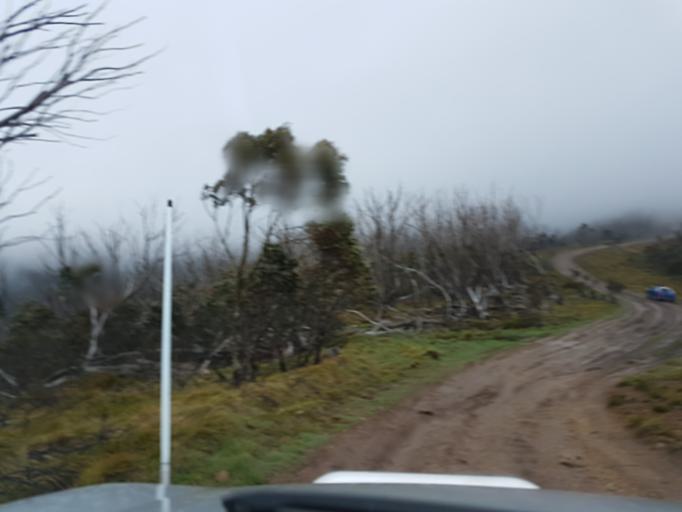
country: AU
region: Victoria
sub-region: Alpine
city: Mount Beauty
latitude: -37.0860
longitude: 147.1073
